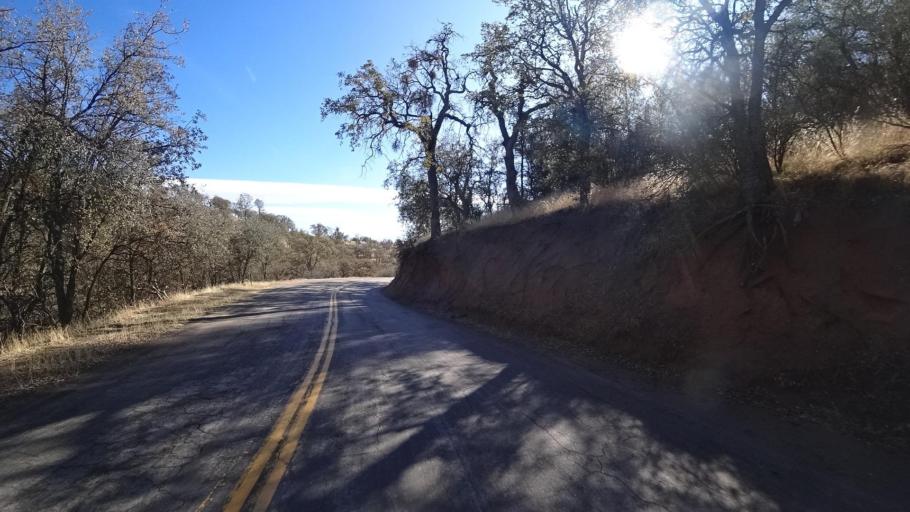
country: US
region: California
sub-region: Kern County
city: Bear Valley Springs
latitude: 35.3518
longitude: -118.5691
